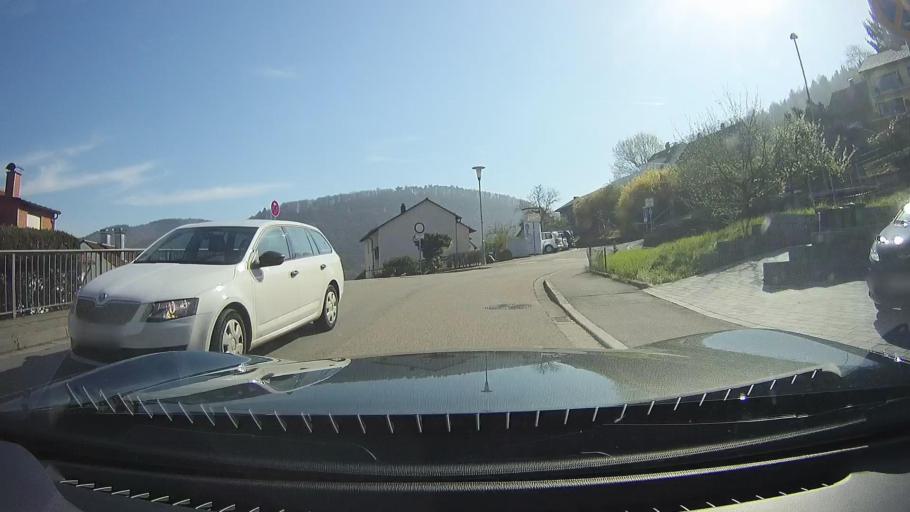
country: DE
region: Baden-Wuerttemberg
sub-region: Karlsruhe Region
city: Eberbach
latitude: 49.4559
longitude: 8.9830
